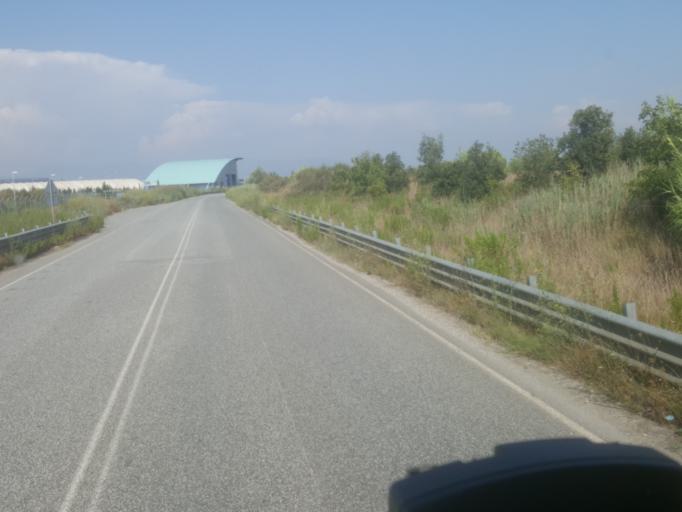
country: IT
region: Tuscany
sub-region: Provincia di Livorno
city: Guasticce
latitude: 43.6020
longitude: 10.4026
